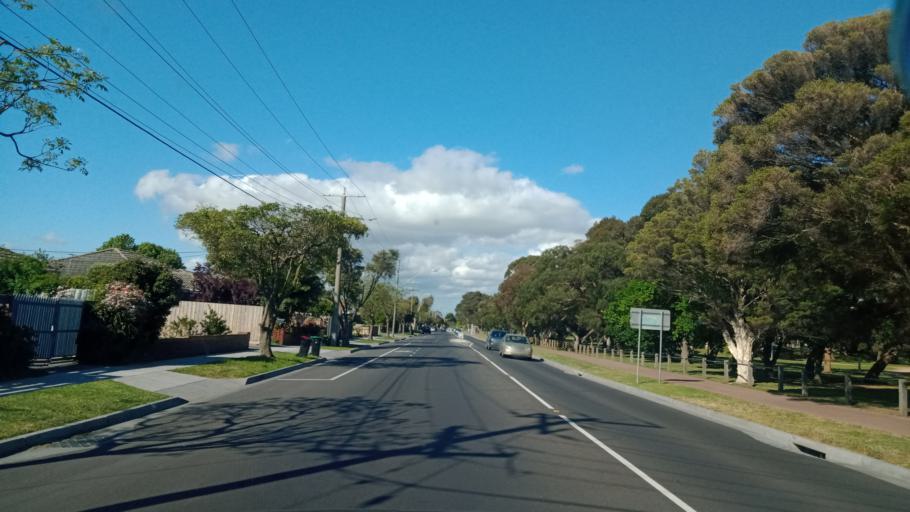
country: AU
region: Victoria
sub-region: Kingston
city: Chelsea
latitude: -38.0478
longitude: 145.1253
